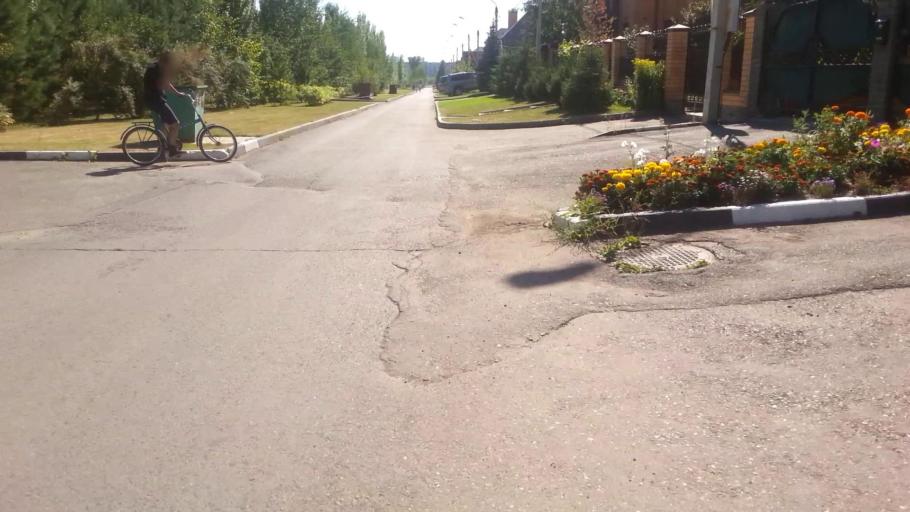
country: RU
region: Altai Krai
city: Novosilikatnyy
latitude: 53.3554
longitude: 83.6568
